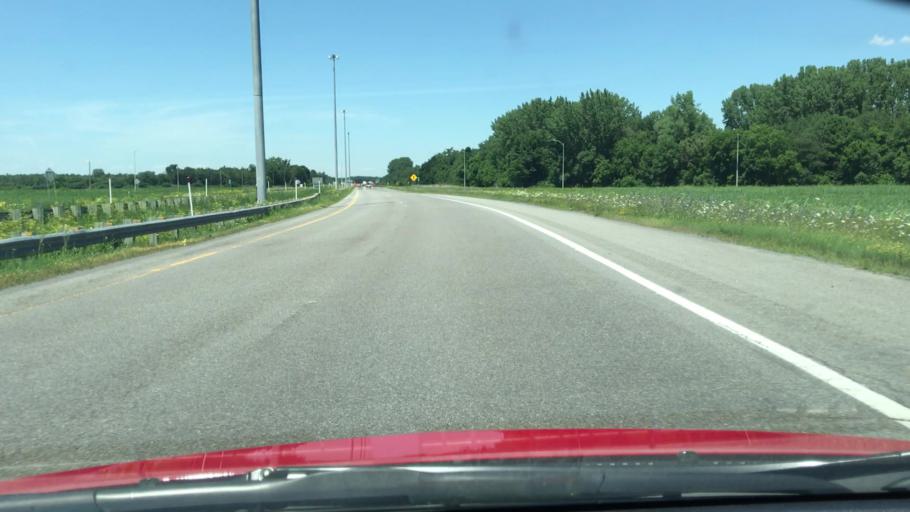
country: US
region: New York
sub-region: Clinton County
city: Champlain
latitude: 45.0695
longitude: -73.4547
